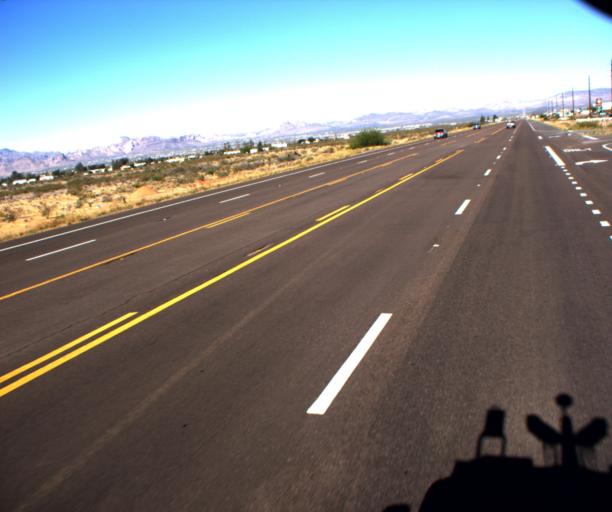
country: US
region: Arizona
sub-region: Mohave County
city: Golden Valley
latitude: 35.2217
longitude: -114.2085
